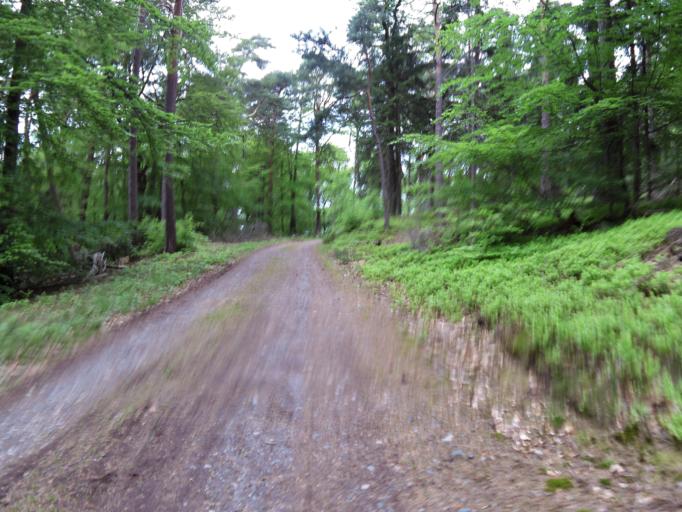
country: DE
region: Rheinland-Pfalz
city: Neidenfels
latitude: 49.4118
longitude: 8.0672
